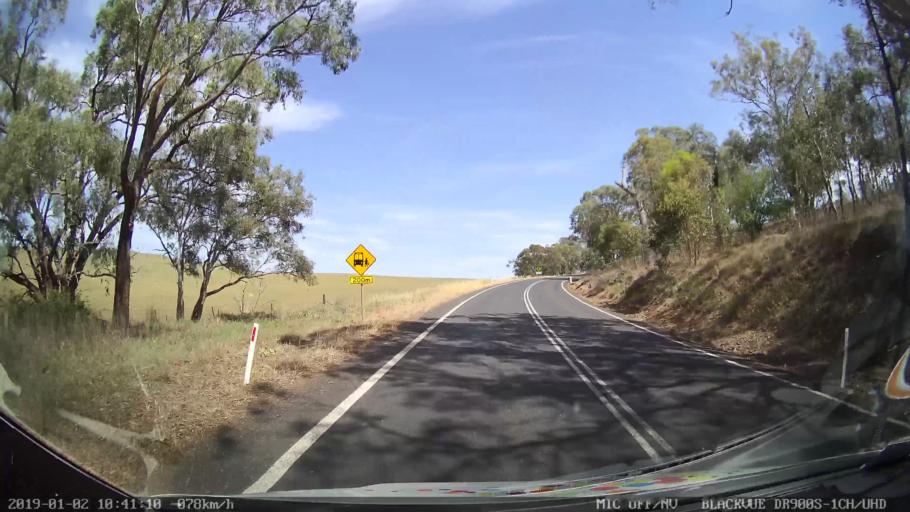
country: AU
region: New South Wales
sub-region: Cootamundra
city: Cootamundra
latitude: -34.7967
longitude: 148.3080
